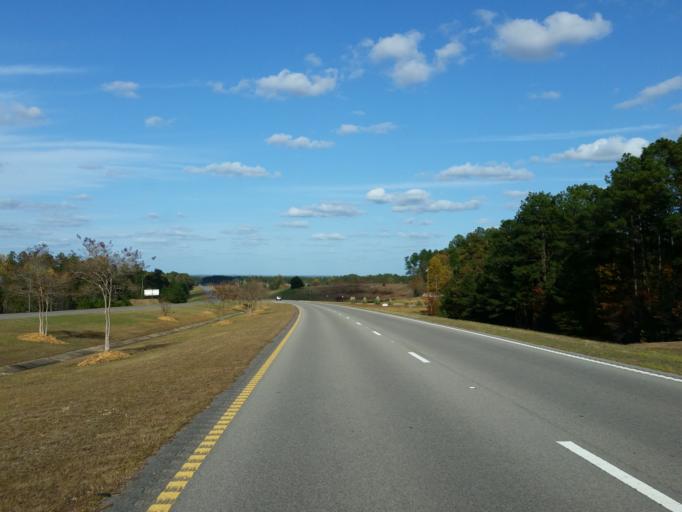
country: US
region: Mississippi
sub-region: Lamar County
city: West Hattiesburg
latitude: 31.2699
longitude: -89.3317
